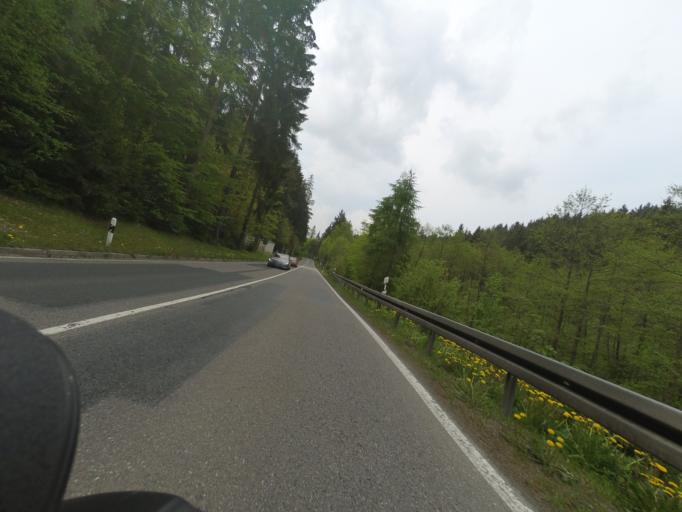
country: DE
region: Saxony
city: Pobershau
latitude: 50.6557
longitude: 13.1963
